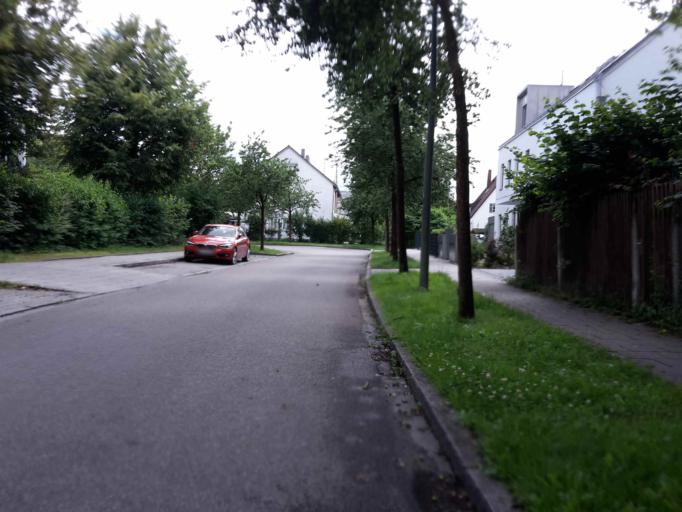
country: DE
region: Bavaria
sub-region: Upper Bavaria
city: Karlsfeld
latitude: 48.1845
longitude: 11.4753
